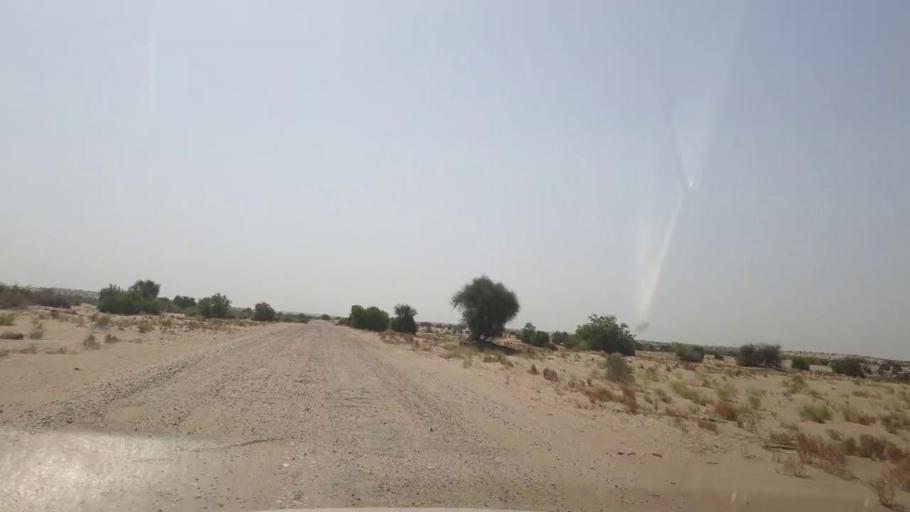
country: PK
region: Sindh
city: Khanpur
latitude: 27.4318
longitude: 69.2526
